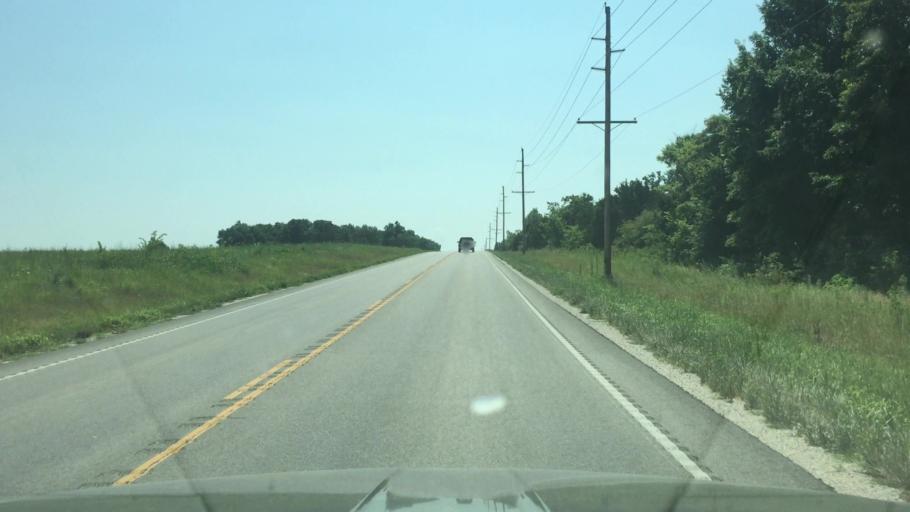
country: US
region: Missouri
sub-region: Miller County
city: Eldon
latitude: 38.3889
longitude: -92.7015
